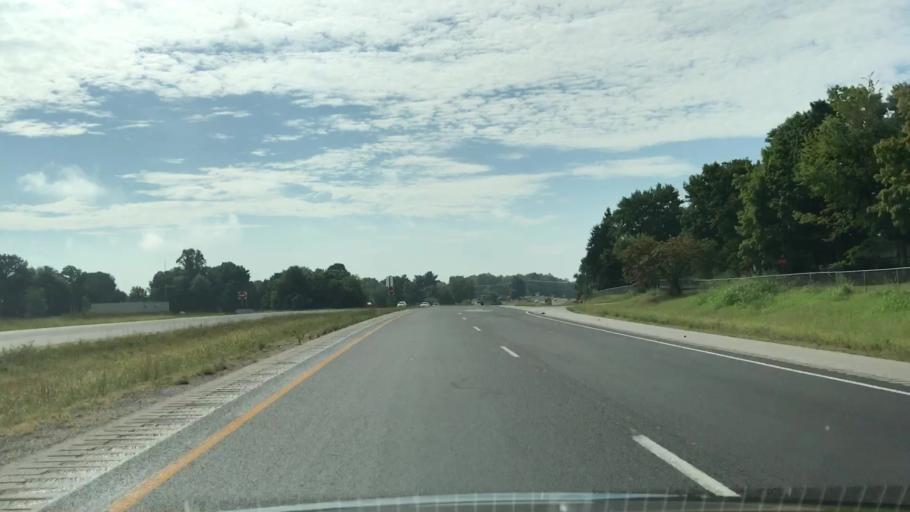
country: US
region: Kentucky
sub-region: Warren County
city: Plano
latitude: 36.8786
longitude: -86.3572
